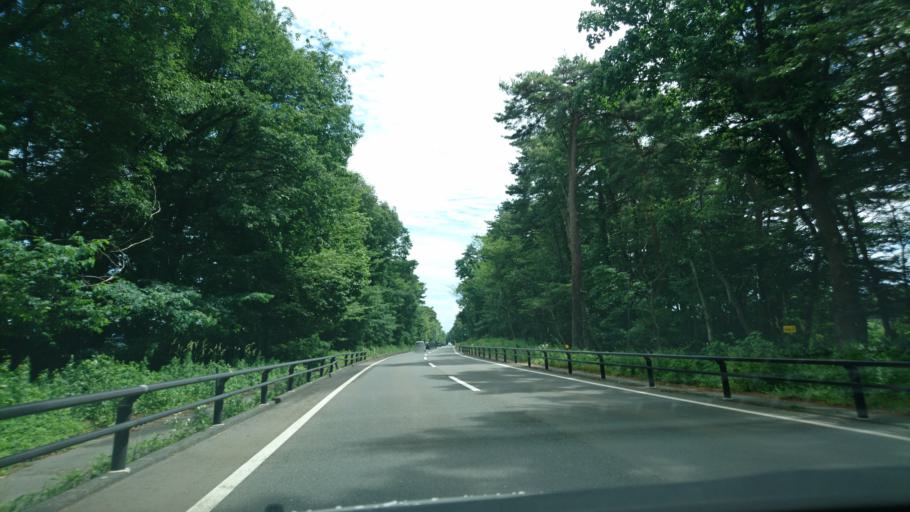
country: JP
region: Iwate
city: Morioka-shi
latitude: 39.7853
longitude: 141.1250
